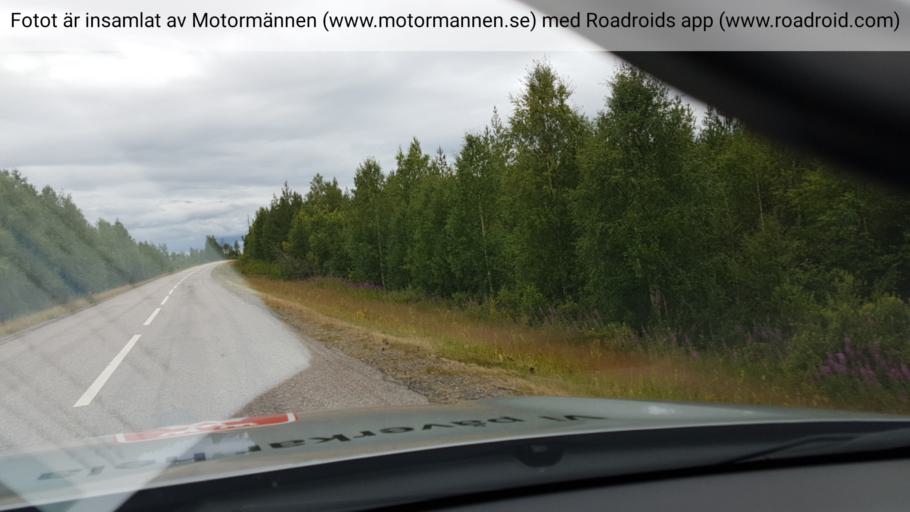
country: SE
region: Norrbotten
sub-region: Pajala Kommun
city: Pajala
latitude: 66.8262
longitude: 23.0263
